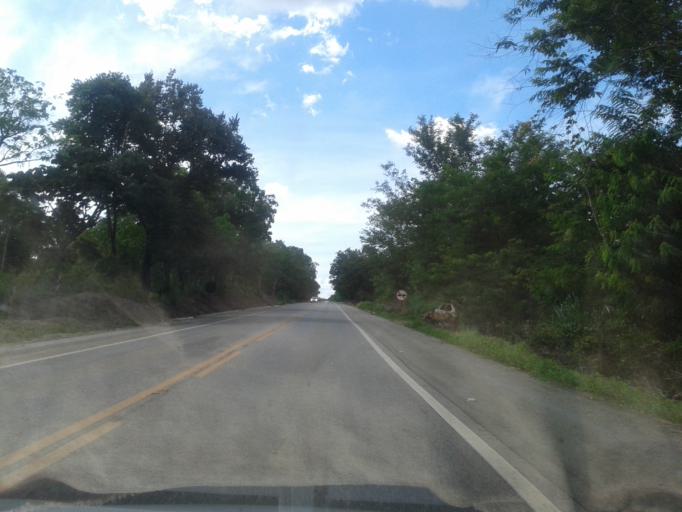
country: BR
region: Goias
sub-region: Itapuranga
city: Itapuranga
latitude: -15.4790
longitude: -50.3350
